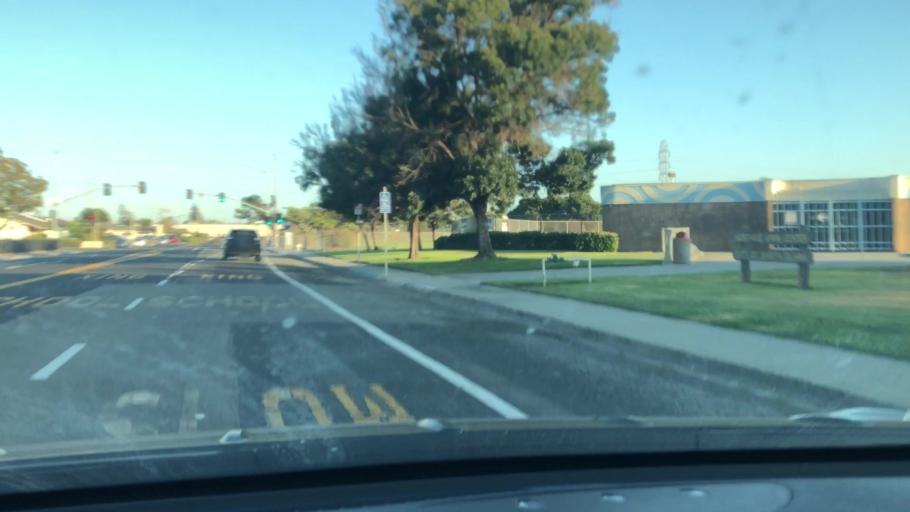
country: US
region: California
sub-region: Santa Clara County
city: Santa Clara
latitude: 37.3905
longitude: -121.9454
